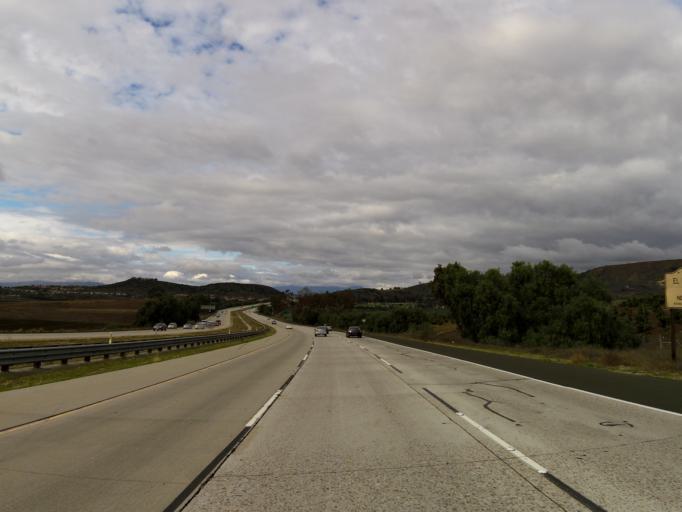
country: US
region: California
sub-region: Ventura County
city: Moorpark
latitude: 34.2579
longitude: -118.8417
